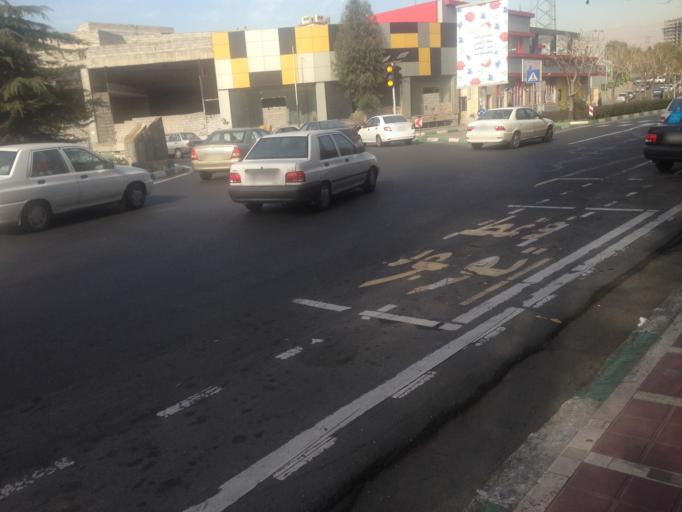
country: IR
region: Tehran
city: Tehran
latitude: 35.7128
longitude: 51.3102
